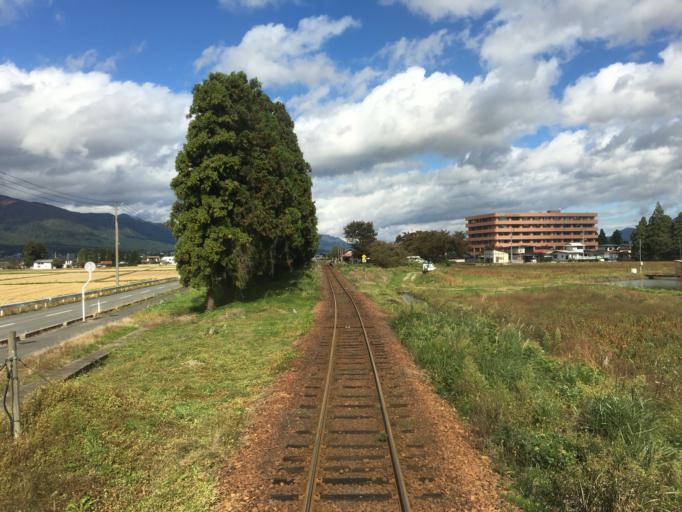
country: JP
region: Yamagata
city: Nagai
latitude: 38.1291
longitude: 140.0345
